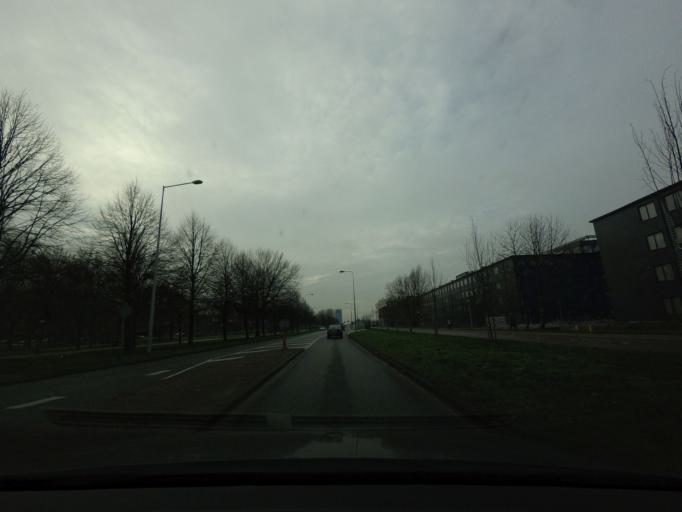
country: NL
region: North Holland
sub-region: Gemeente Amsterdam
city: Amsterdam-Zuidoost
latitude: 52.2971
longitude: 4.9570
